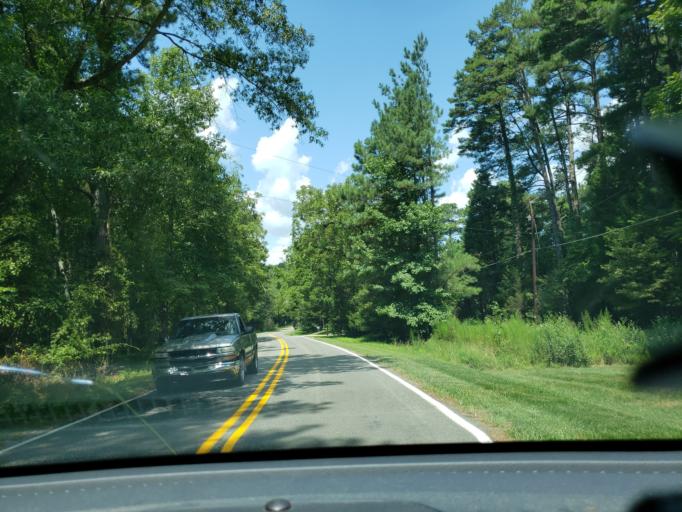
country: US
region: North Carolina
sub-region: Orange County
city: Hillsborough
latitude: 36.0725
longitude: -78.9992
